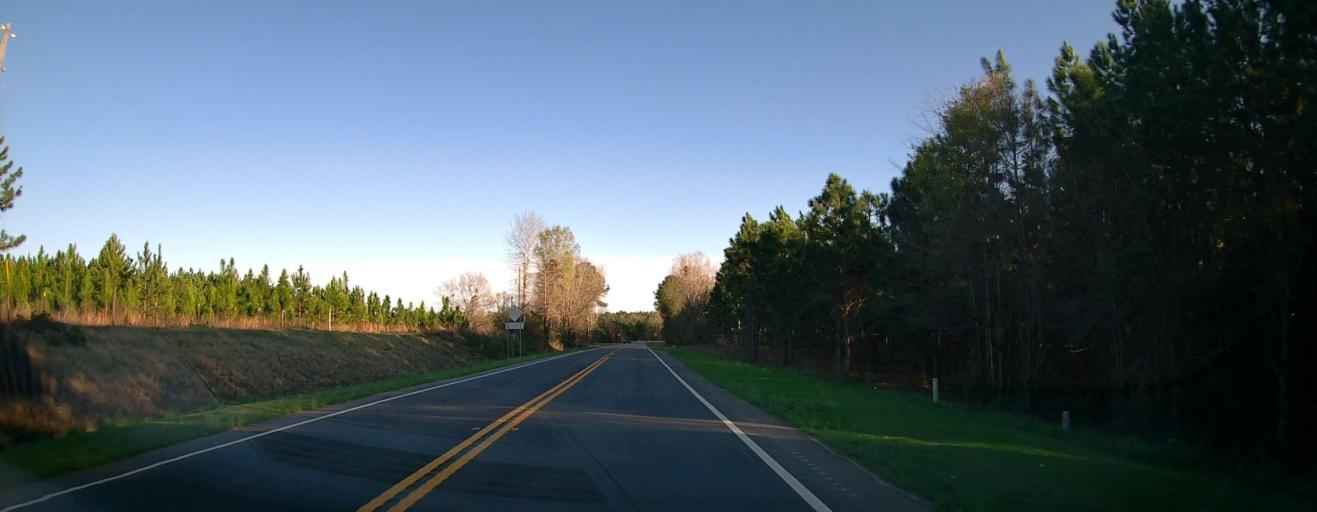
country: US
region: Georgia
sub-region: Wilcox County
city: Abbeville
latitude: 32.0830
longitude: -83.2899
